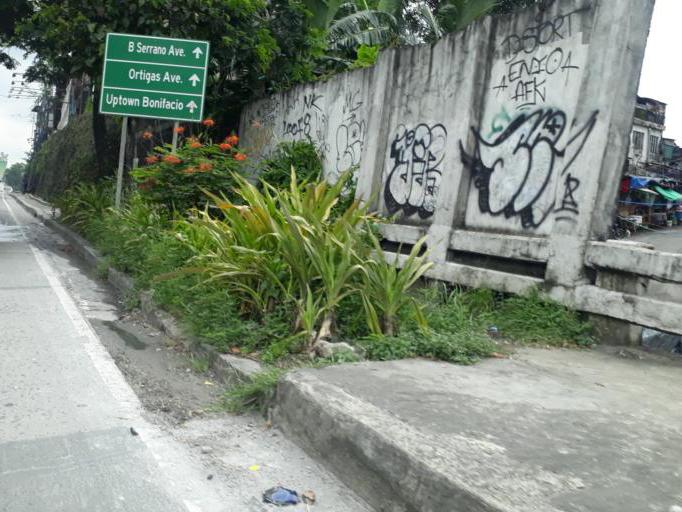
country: PH
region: Metro Manila
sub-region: Marikina
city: Calumpang
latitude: 14.6258
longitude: 121.0742
